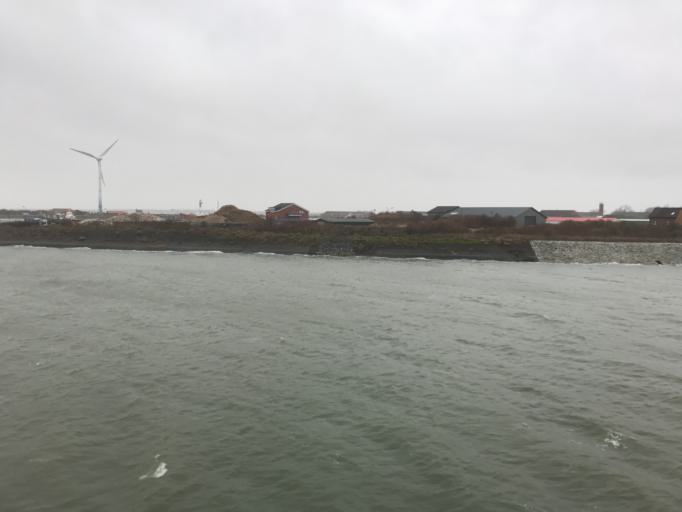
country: DE
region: Lower Saxony
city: Borkum
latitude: 53.5594
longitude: 6.7556
